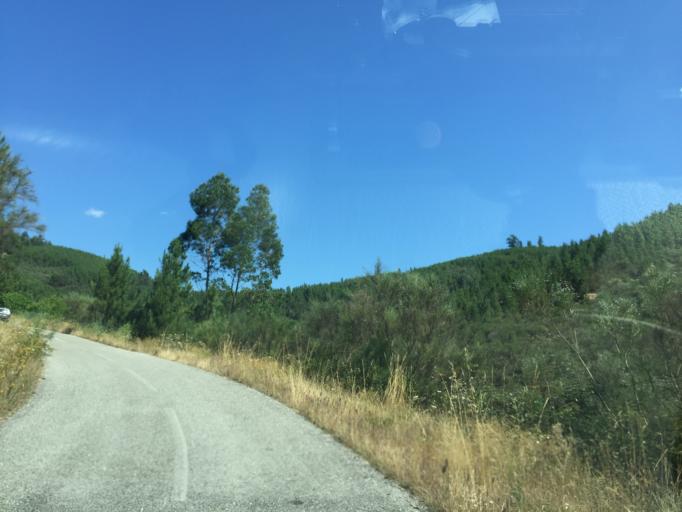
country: PT
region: Coimbra
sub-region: Pampilhosa da Serra
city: Pampilhosa da Serra
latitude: 40.0818
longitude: -7.8172
